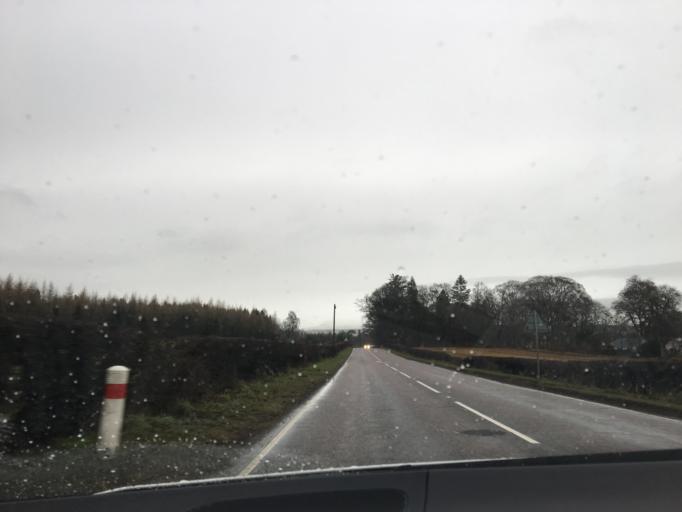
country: GB
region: Scotland
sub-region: Stirling
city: Doune
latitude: 56.1788
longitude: -4.0636
